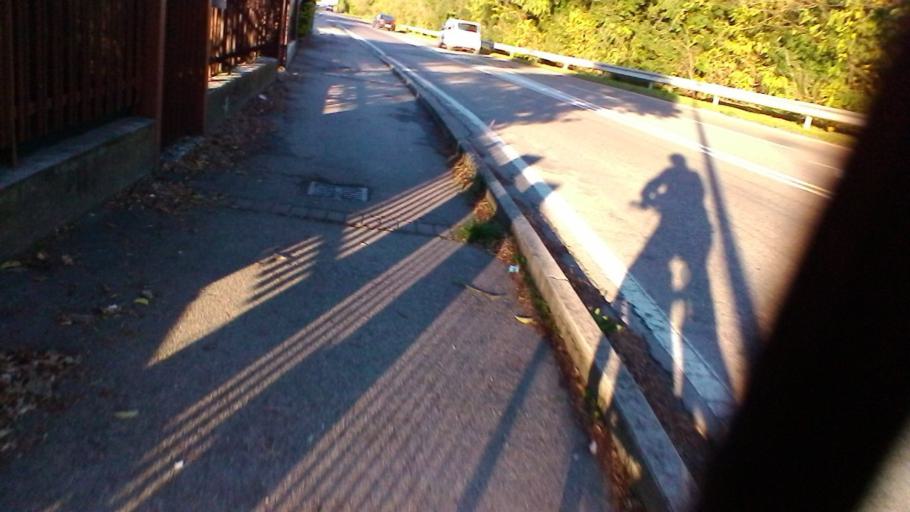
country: IT
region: Veneto
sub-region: Provincia di Verona
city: Povegliano Veronese
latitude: 45.3504
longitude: 10.8884
